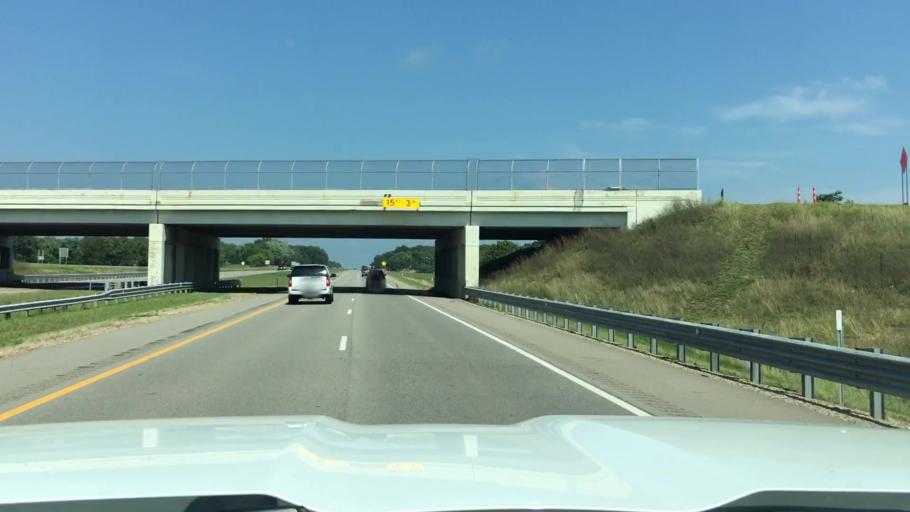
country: US
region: Michigan
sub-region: Kalamazoo County
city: Portage
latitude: 42.1990
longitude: -85.6456
